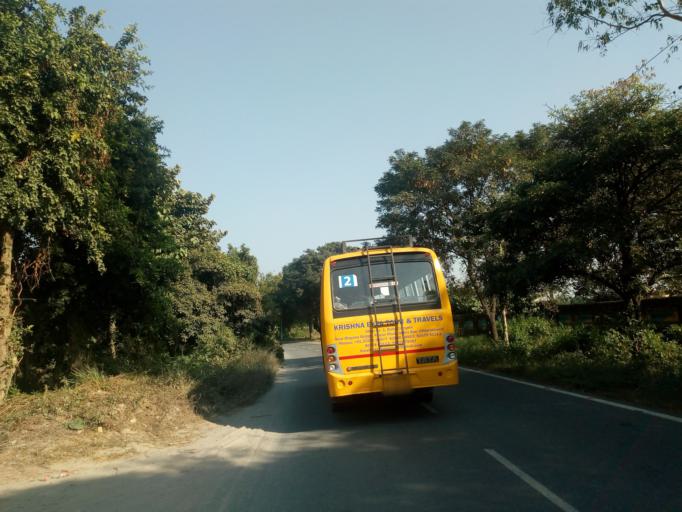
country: IN
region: Uttarakhand
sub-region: Dehradun
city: Harbatpur
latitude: 30.4419
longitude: 77.7055
